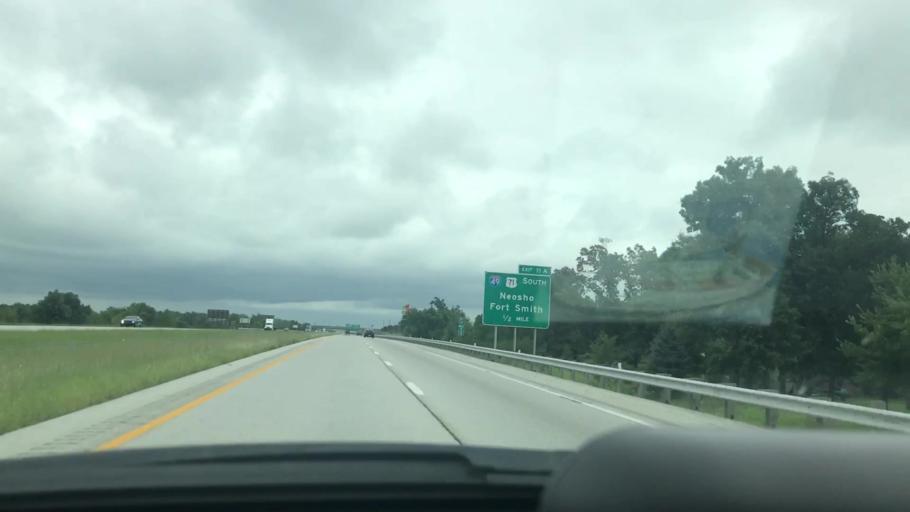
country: US
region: Missouri
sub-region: Jasper County
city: Duquesne
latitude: 37.0567
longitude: -94.4411
